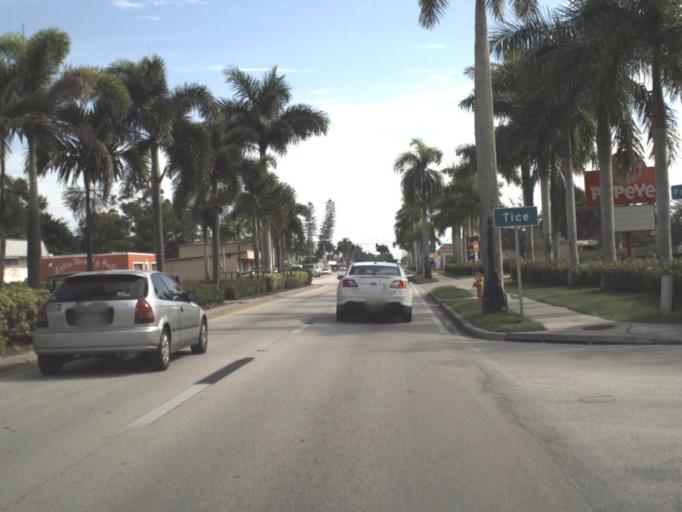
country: US
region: Florida
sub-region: Lee County
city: Tice
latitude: 26.6695
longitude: -81.8247
